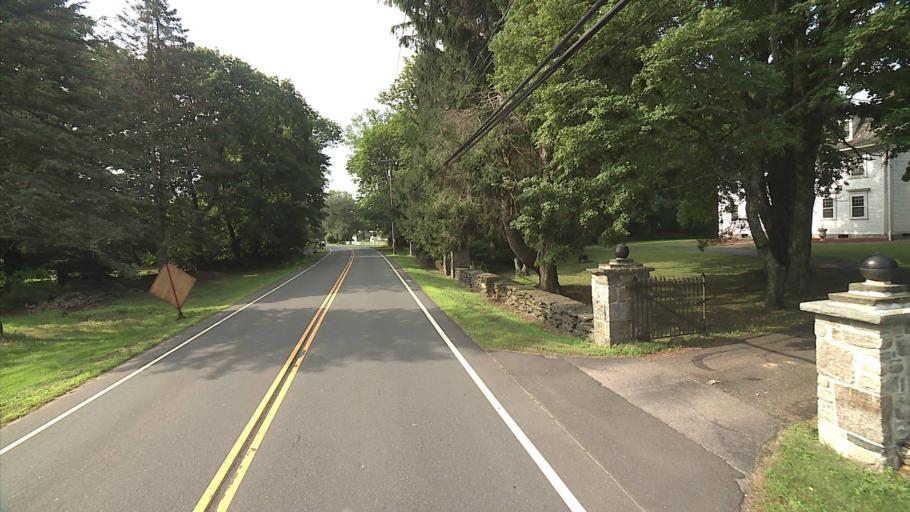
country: US
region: Connecticut
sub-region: Middlesex County
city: Moodus
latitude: 41.5440
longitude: -72.4130
